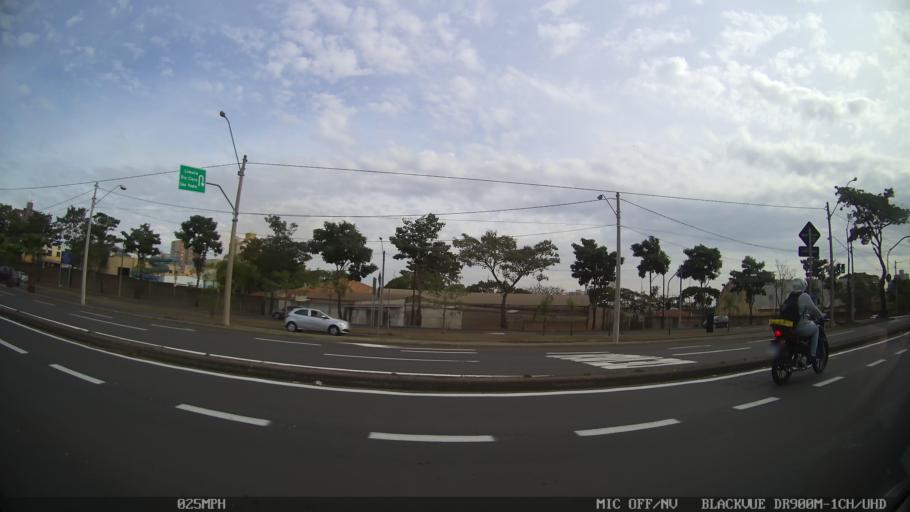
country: BR
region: Sao Paulo
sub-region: Piracicaba
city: Piracicaba
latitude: -22.7450
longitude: -47.6377
